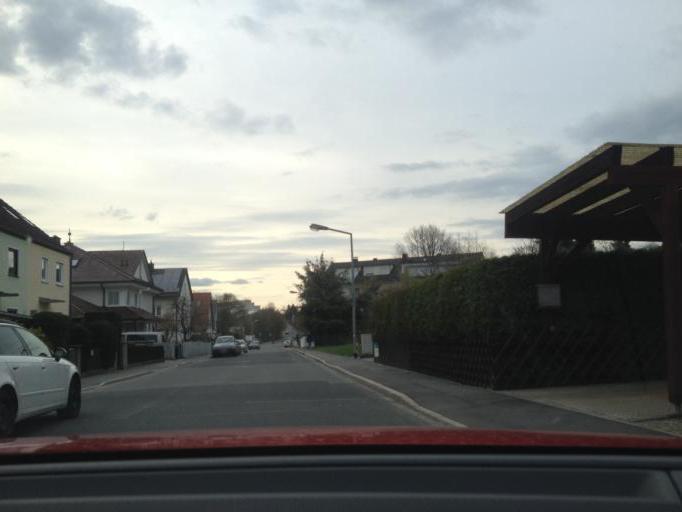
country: DE
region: Bavaria
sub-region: Regierungsbezirk Mittelfranken
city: Lauf an der Pegnitz
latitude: 49.5152
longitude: 11.2747
